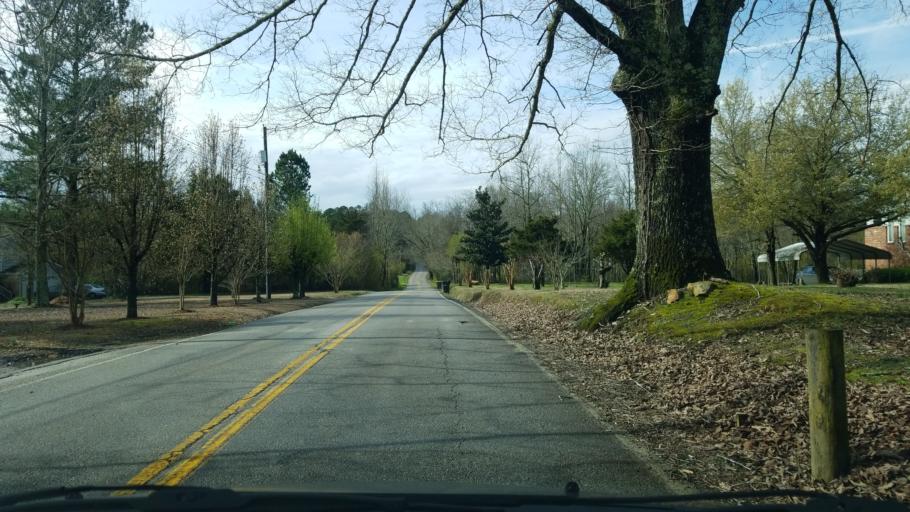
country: US
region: Tennessee
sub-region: Hamilton County
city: Collegedale
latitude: 35.0539
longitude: -85.1006
